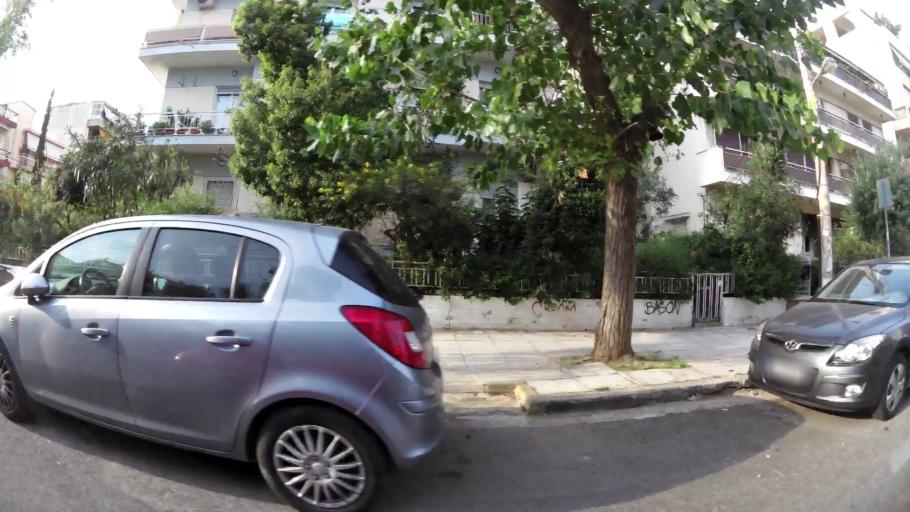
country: GR
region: Attica
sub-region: Nomarchia Athinas
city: Palaio Faliro
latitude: 37.9311
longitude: 23.7010
